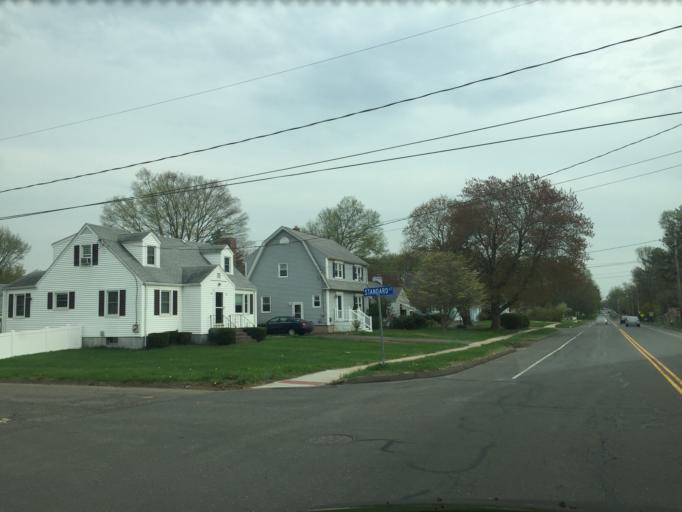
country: US
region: Connecticut
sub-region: Hartford County
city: Newington
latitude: 41.6880
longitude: -72.7440
